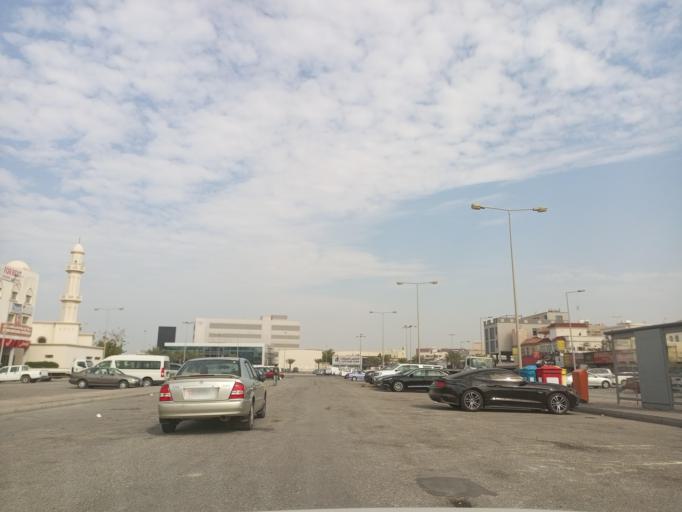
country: BH
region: Muharraq
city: Al Hadd
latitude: 26.2549
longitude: 50.6450
